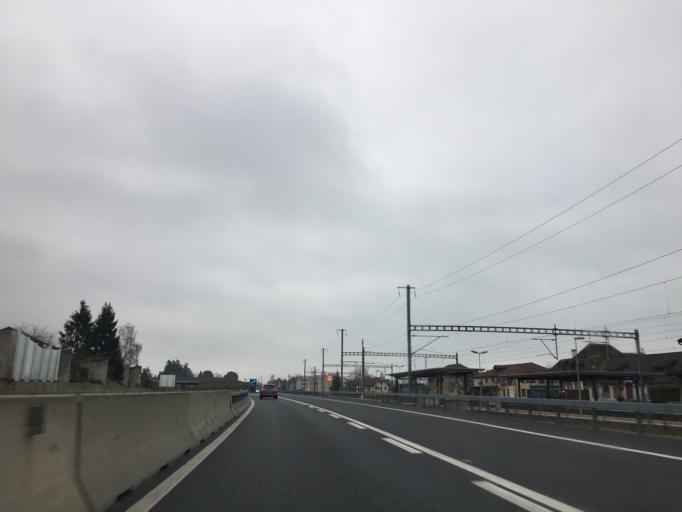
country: CH
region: Neuchatel
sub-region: Neuchatel District
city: Le Landeron
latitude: 47.0569
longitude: 7.0657
